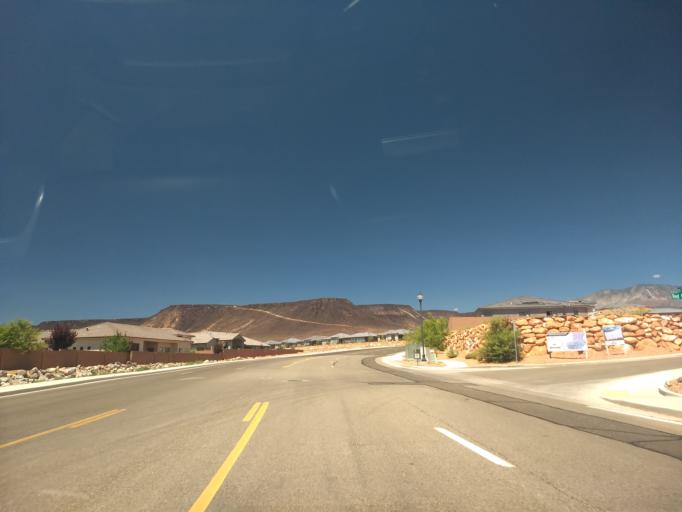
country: US
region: Utah
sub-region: Washington County
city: Washington
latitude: 37.1574
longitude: -113.5260
